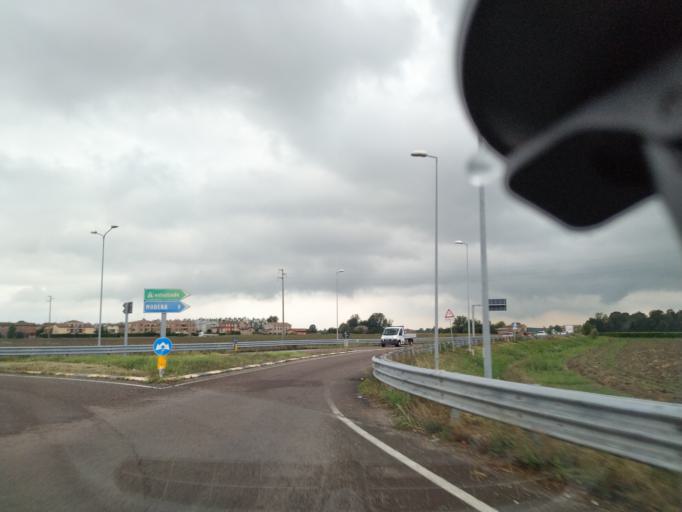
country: IT
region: Emilia-Romagna
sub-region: Provincia di Modena
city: Nonantola
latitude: 44.6856
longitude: 11.0413
